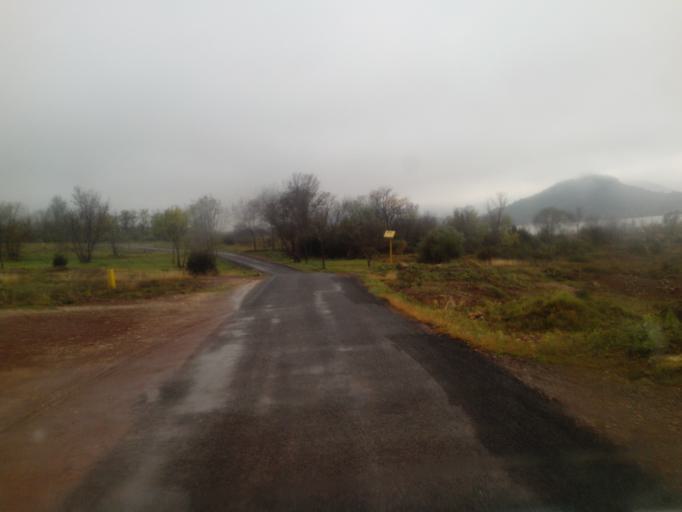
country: FR
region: Languedoc-Roussillon
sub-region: Departement de l'Herault
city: Nebian
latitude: 43.6409
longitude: 3.3771
